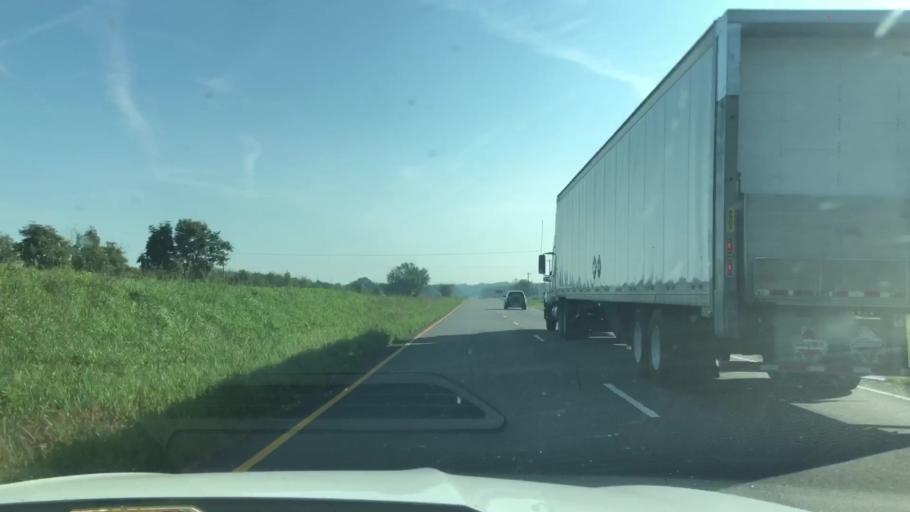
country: US
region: Virginia
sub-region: Essex County
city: Tappahannock
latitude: 37.9514
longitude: -76.8231
